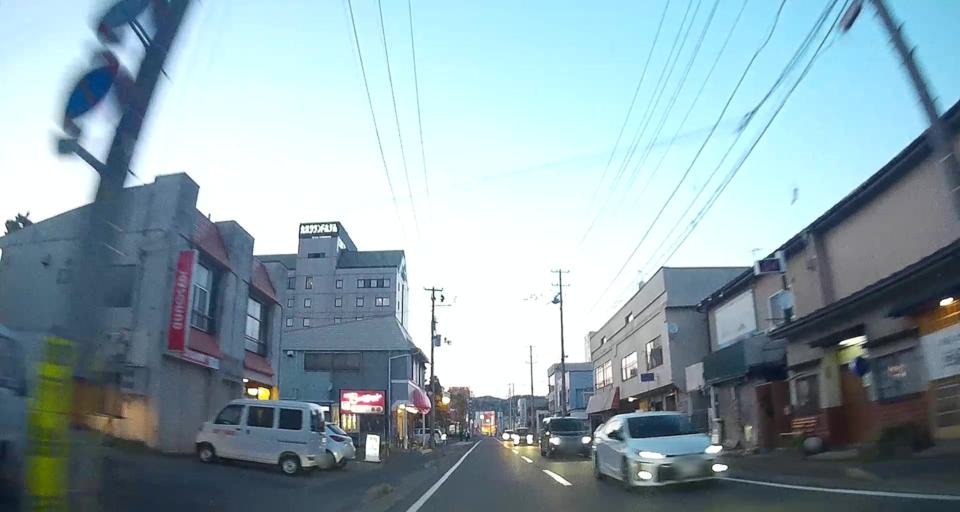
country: JP
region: Aomori
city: Hachinohe
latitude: 40.1891
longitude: 141.7724
